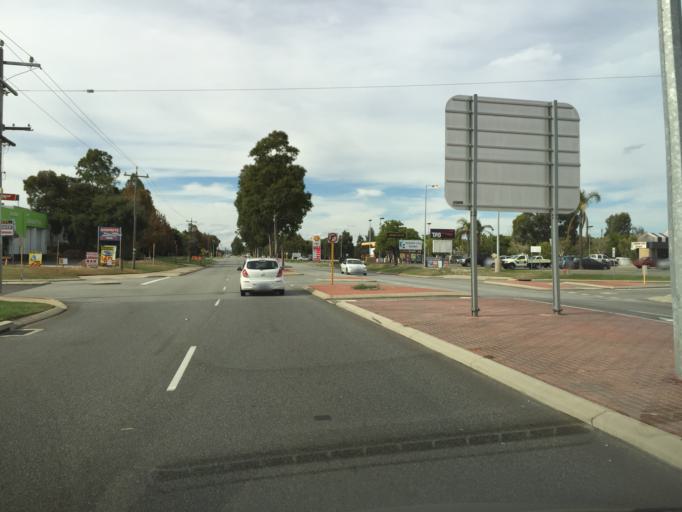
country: AU
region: Western Australia
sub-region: Canning
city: Willetton
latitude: -32.0712
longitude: 115.8939
